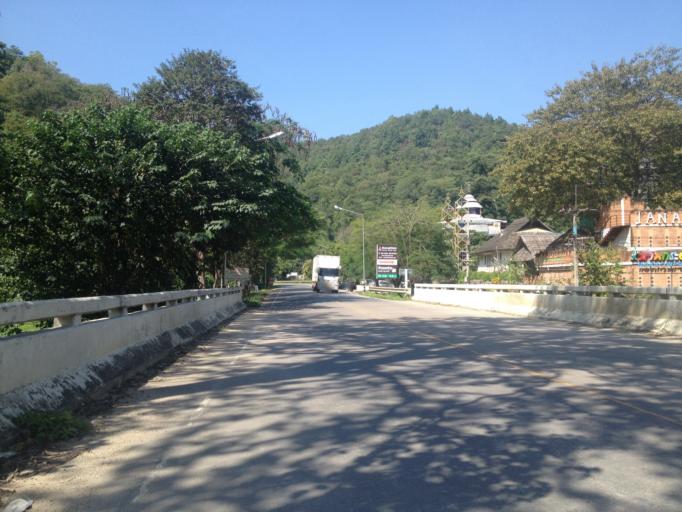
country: TH
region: Chiang Mai
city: Hang Dong
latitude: 18.7374
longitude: 98.8990
